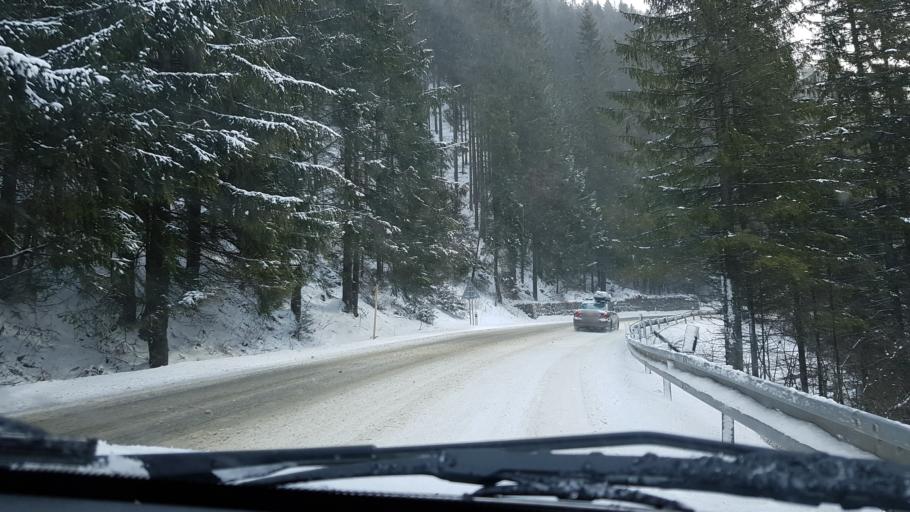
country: SK
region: Presovsky
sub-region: Okres Poprad
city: Zdiar
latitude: 49.2632
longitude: 20.3003
